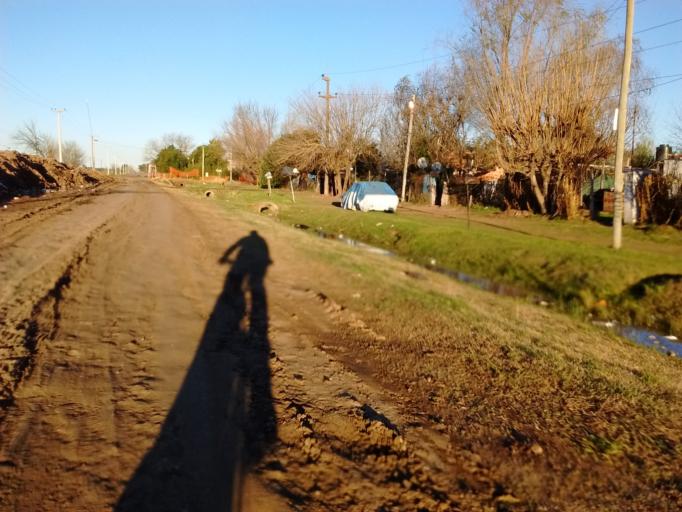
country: AR
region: Santa Fe
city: Funes
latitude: -32.9093
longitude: -60.8554
